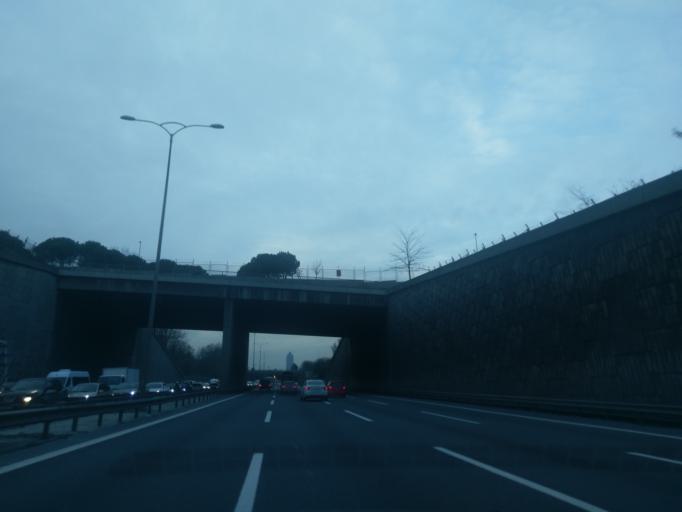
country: TR
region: Istanbul
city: Sisli
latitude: 41.0959
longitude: 29.0183
